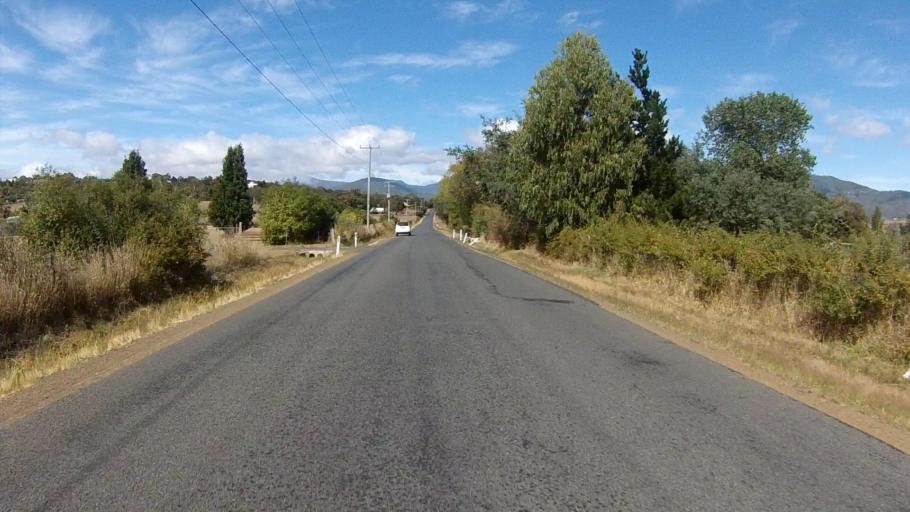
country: AU
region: Tasmania
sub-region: Brighton
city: Old Beach
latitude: -42.7638
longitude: 147.2776
